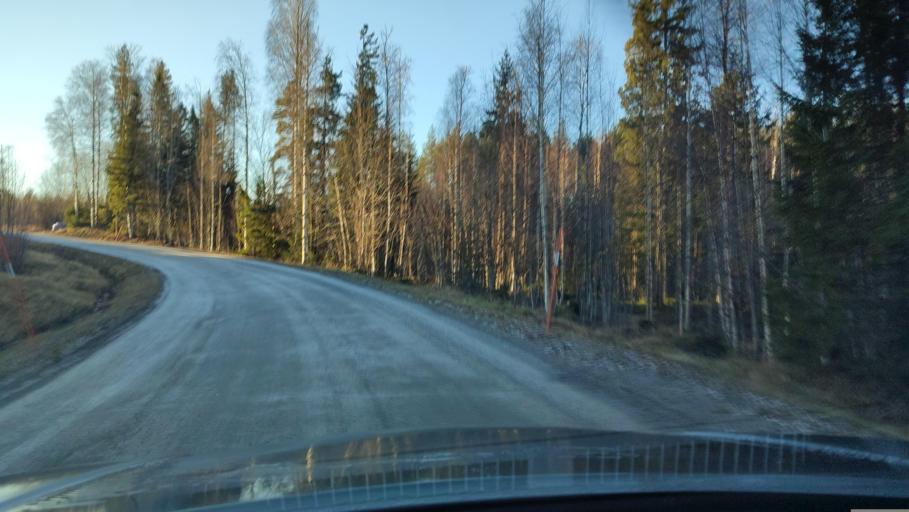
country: SE
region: Vaesterbotten
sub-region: Skelleftea Kommun
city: Viken
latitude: 64.7205
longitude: 20.9163
